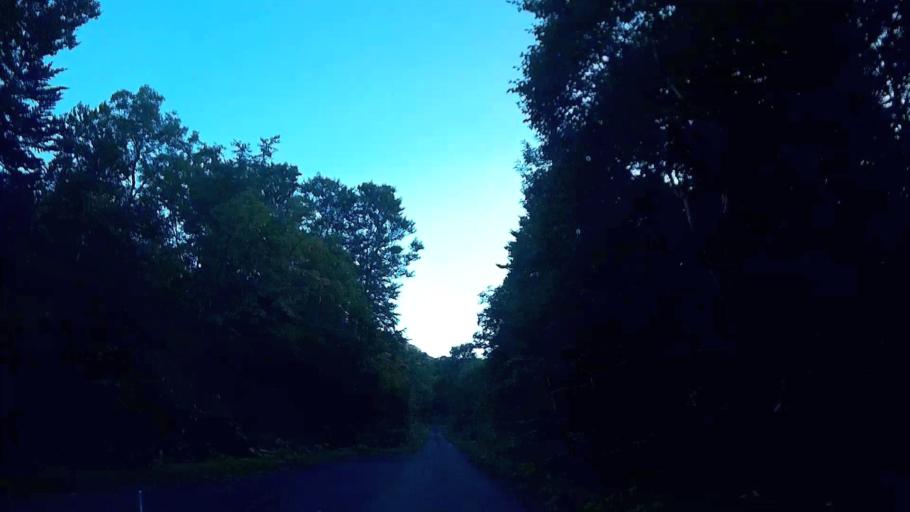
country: JP
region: Hokkaido
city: Iwanai
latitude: 42.5990
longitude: 139.9834
